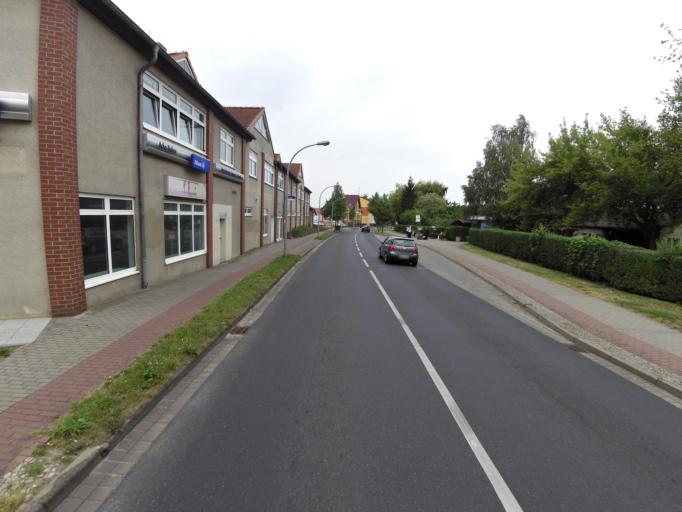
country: DE
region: Brandenburg
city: Zehdenick
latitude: 52.9768
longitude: 13.3295
